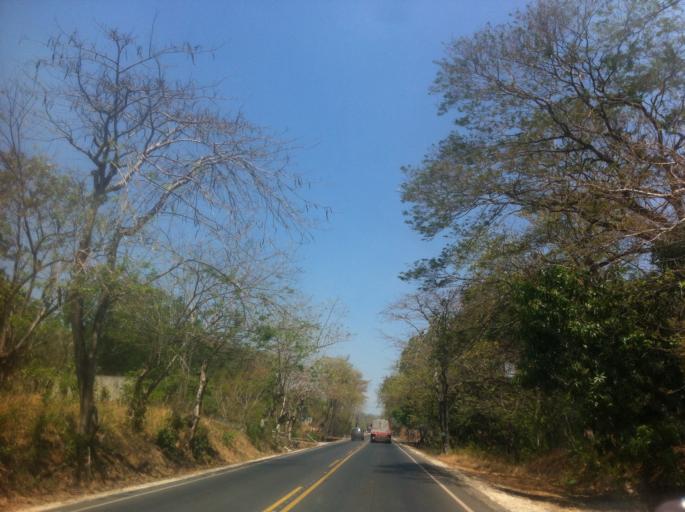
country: CR
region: Guanacaste
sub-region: Canton de Nicoya
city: Nicoya
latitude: 10.2035
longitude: -85.4945
